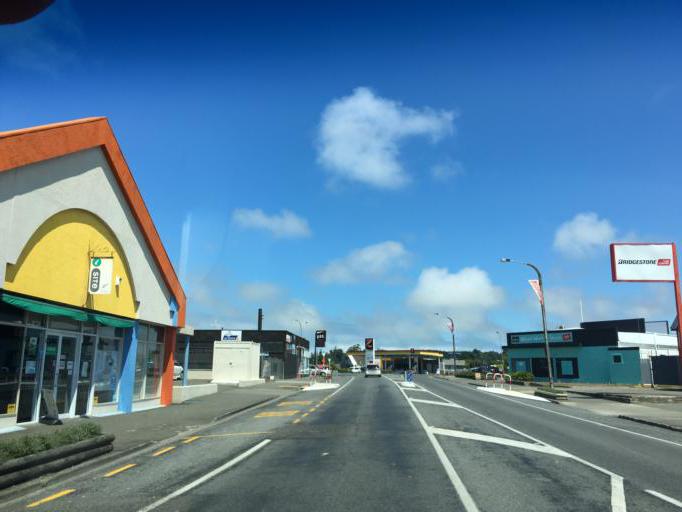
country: NZ
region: Hawke's Bay
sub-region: Wairoa District
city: Wairoa
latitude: -39.0343
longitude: 177.4183
